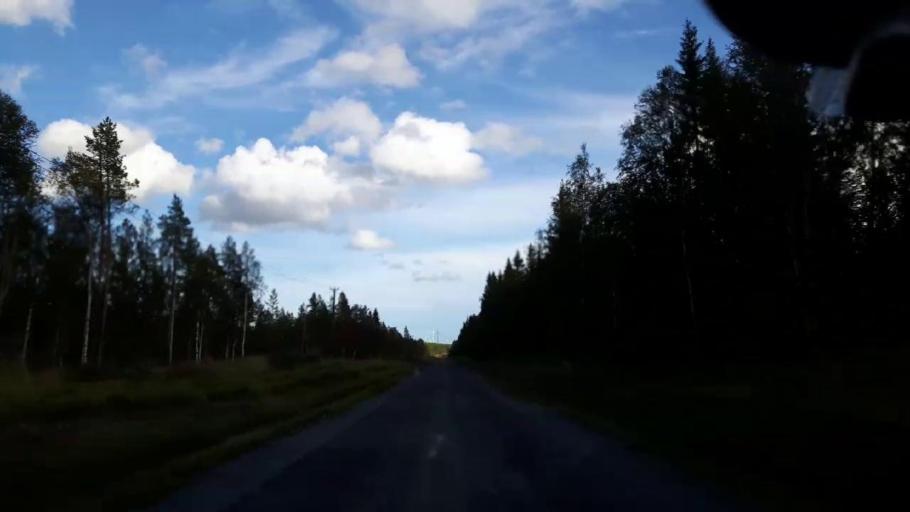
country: SE
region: Jaemtland
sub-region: Ragunda Kommun
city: Hammarstrand
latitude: 63.4376
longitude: 16.0074
